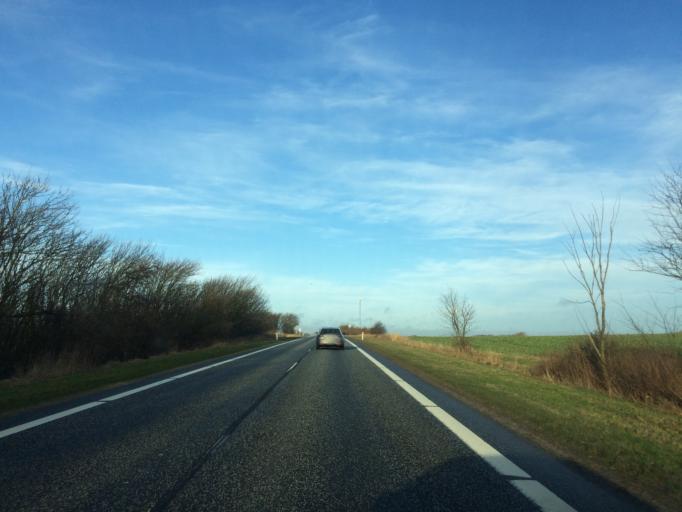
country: DK
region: North Denmark
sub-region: Thisted Kommune
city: Hurup
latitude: 56.7872
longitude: 8.4680
